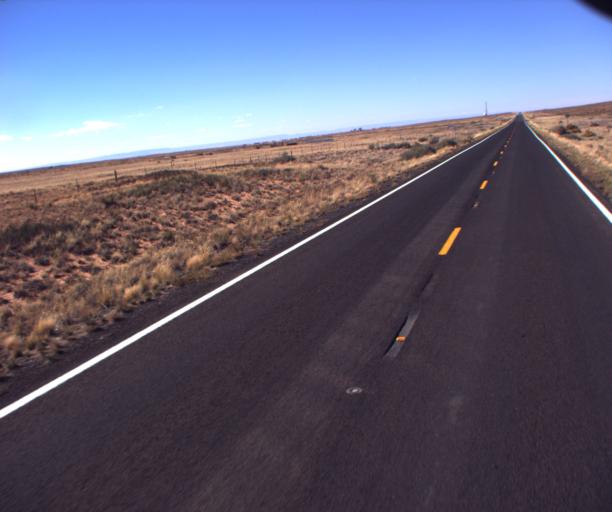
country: US
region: Arizona
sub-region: Coconino County
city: Tuba City
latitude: 35.9845
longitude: -110.9972
